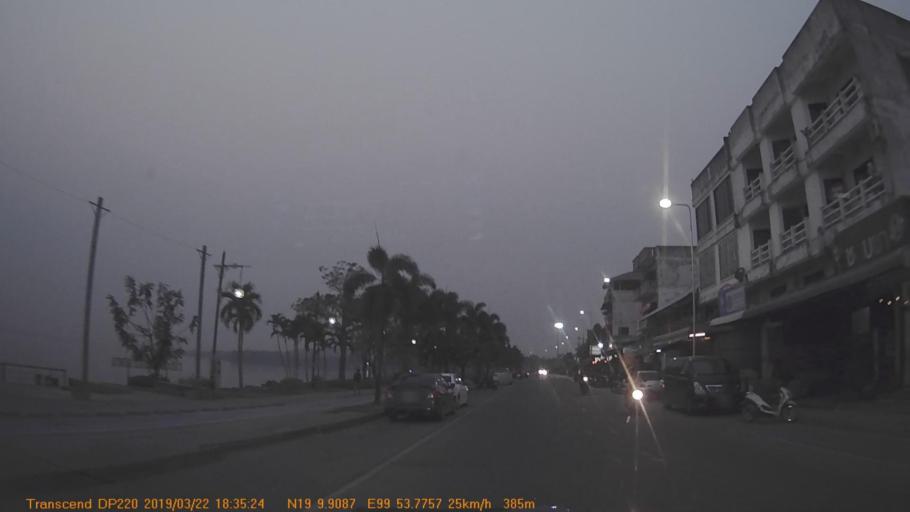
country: TH
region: Phayao
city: Phayao
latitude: 19.1652
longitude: 99.8962
